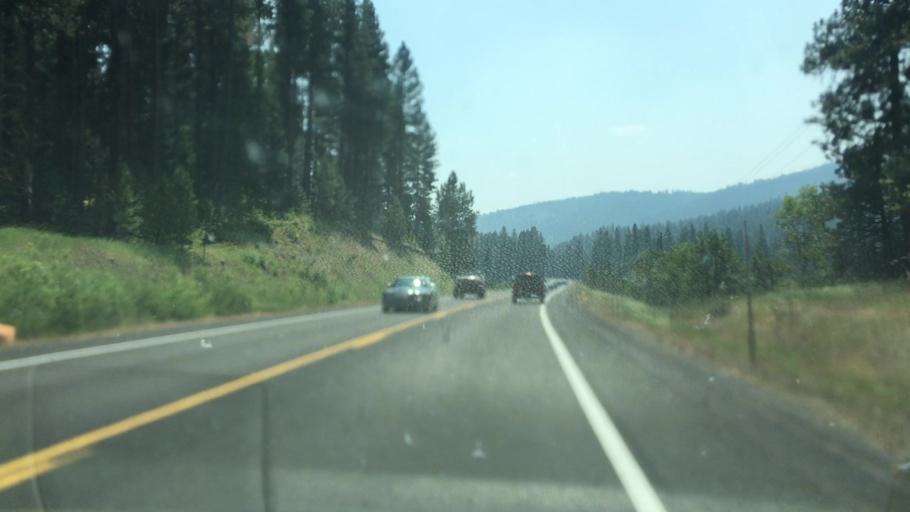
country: US
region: Idaho
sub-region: Valley County
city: McCall
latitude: 45.1048
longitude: -116.3037
